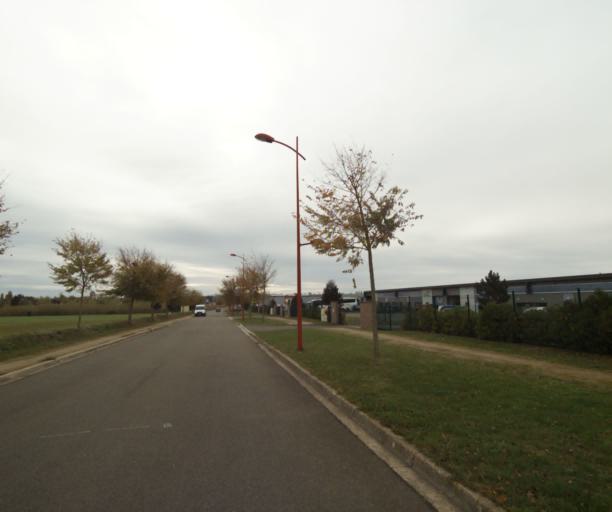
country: FR
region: Centre
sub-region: Departement d'Eure-et-Loir
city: Dreux
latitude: 48.7544
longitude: 1.3532
